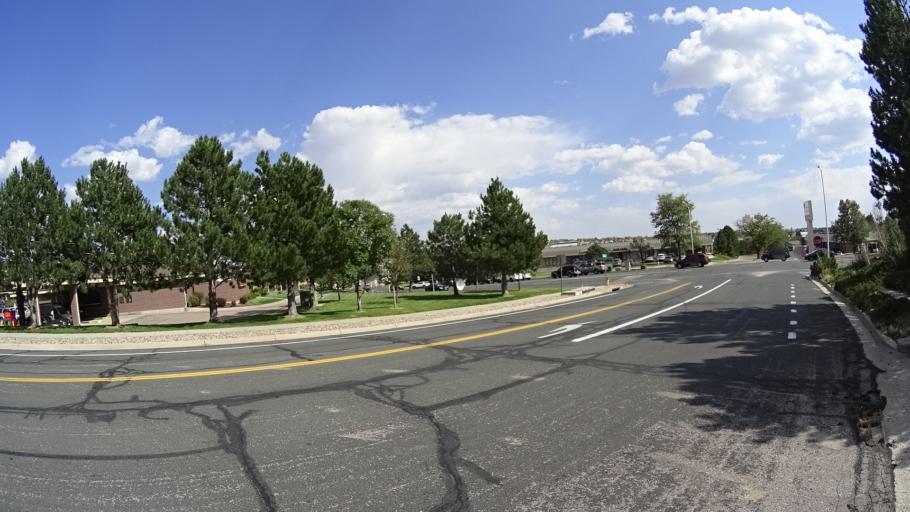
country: US
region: Colorado
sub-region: El Paso County
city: Cimarron Hills
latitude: 38.8720
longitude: -104.7231
